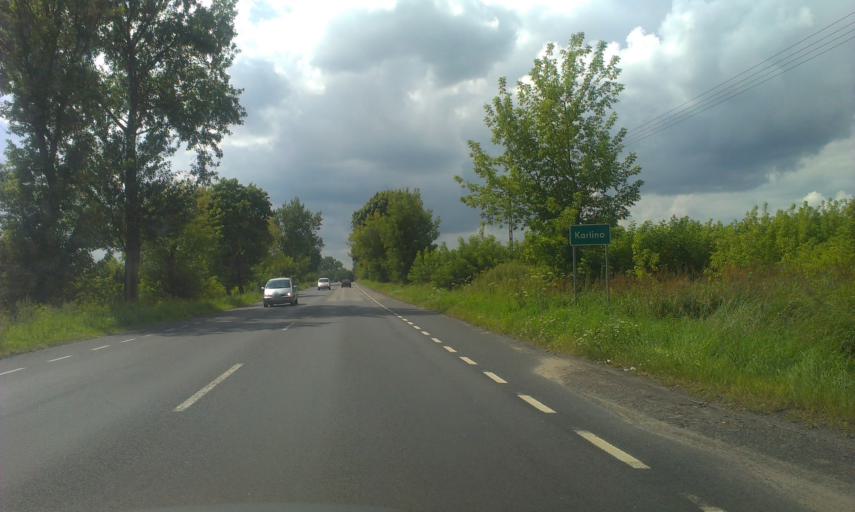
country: PL
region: West Pomeranian Voivodeship
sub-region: Powiat bialogardzki
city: Karlino
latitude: 54.0463
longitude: 15.8936
